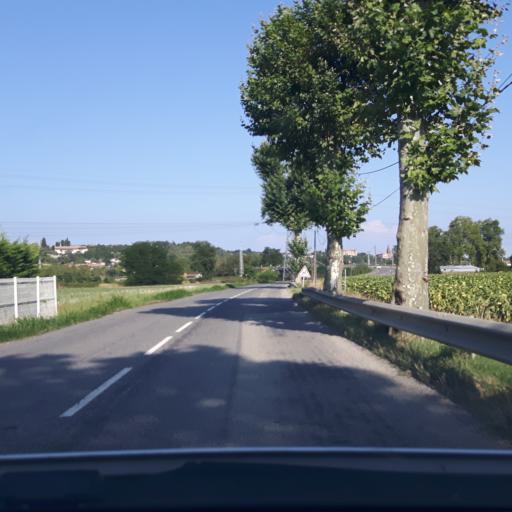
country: FR
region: Midi-Pyrenees
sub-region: Departement de la Haute-Garonne
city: Castelnau-d'Estretefonds
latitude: 43.7877
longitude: 1.3355
